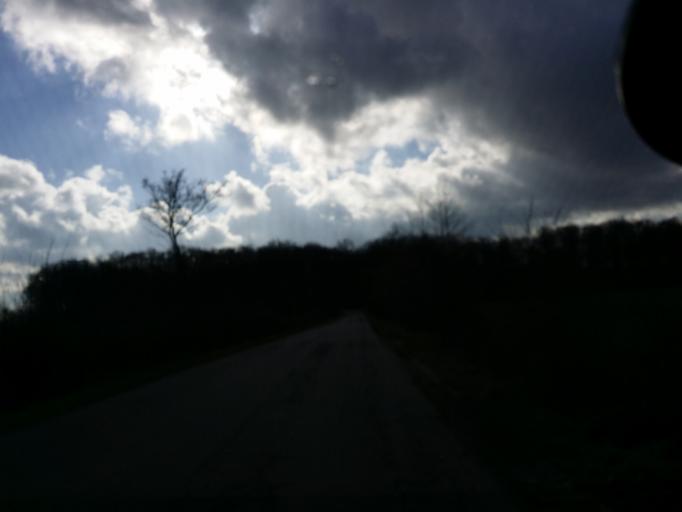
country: DE
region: Schleswig-Holstein
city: Westensee
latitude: 54.3048
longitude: 9.9070
